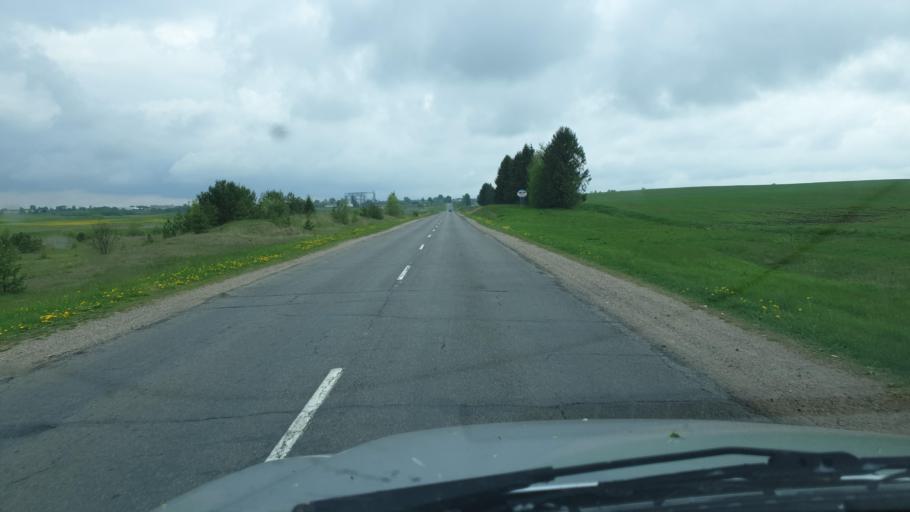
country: BY
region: Vitebsk
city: Lyepyel'
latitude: 54.8835
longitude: 28.6494
